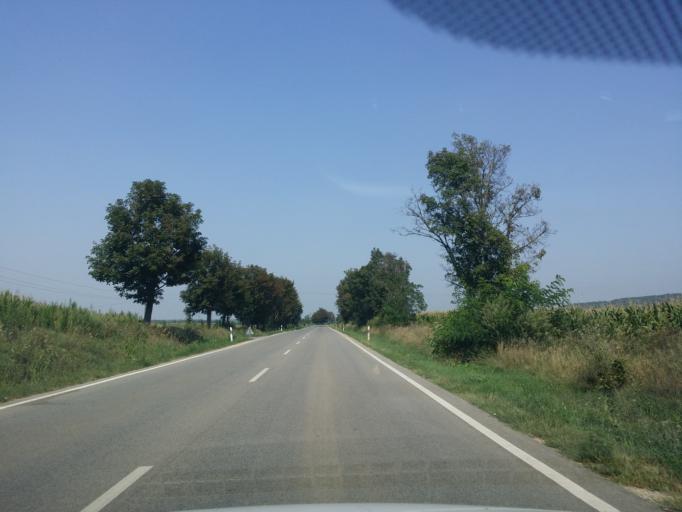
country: HU
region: Tolna
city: Simontornya
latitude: 46.7304
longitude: 18.4977
